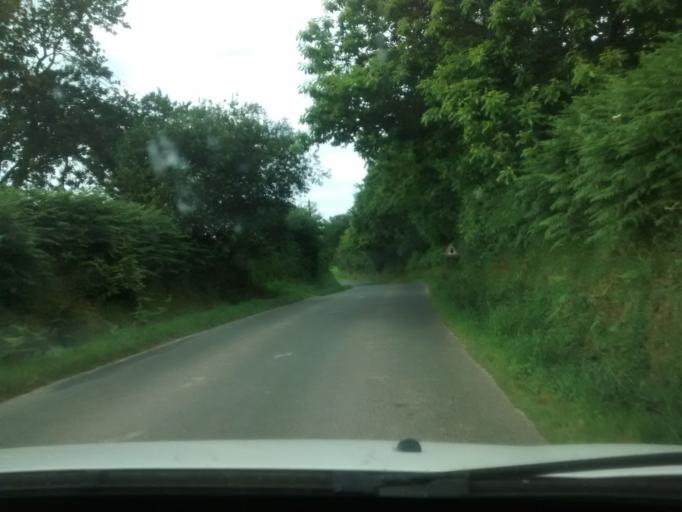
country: FR
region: Brittany
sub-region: Departement des Cotes-d'Armor
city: Trelevern
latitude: 48.8031
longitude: -3.3648
